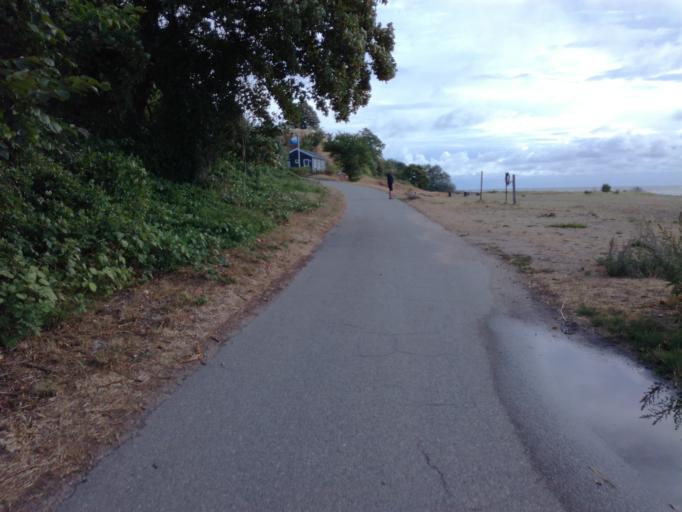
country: DK
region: South Denmark
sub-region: Fredericia Kommune
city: Fredericia
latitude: 55.5796
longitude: 9.7850
